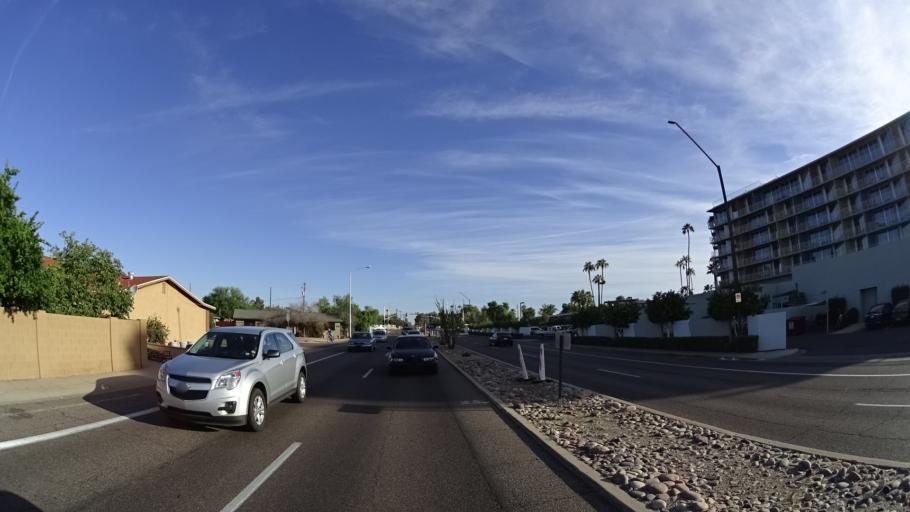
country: US
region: Arizona
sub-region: Maricopa County
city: Paradise Valley
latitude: 33.4931
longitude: -111.9348
